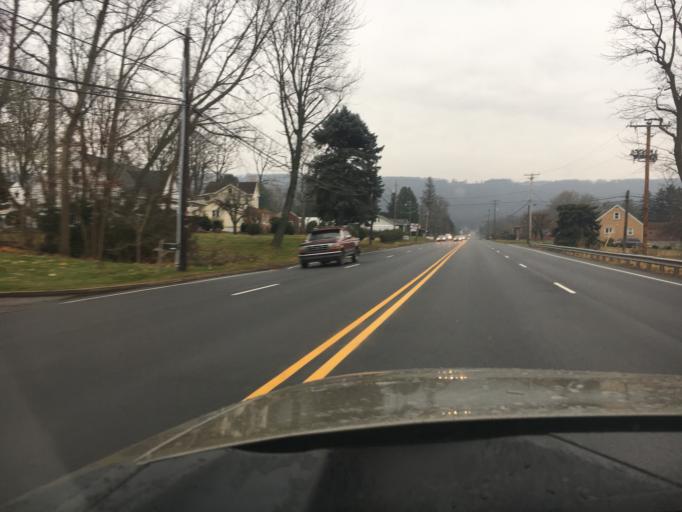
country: US
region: Pennsylvania
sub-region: Luzerne County
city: Harleigh
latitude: 41.0199
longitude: -75.9641
